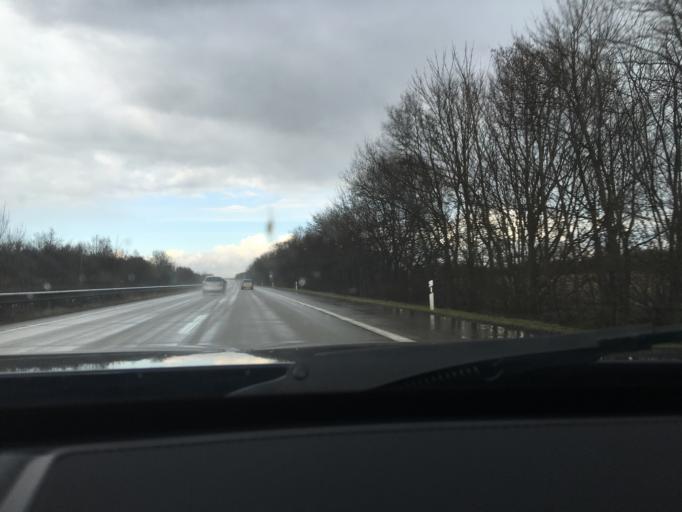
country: DE
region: Lower Saxony
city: Loxstedt
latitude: 53.4864
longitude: 8.6224
